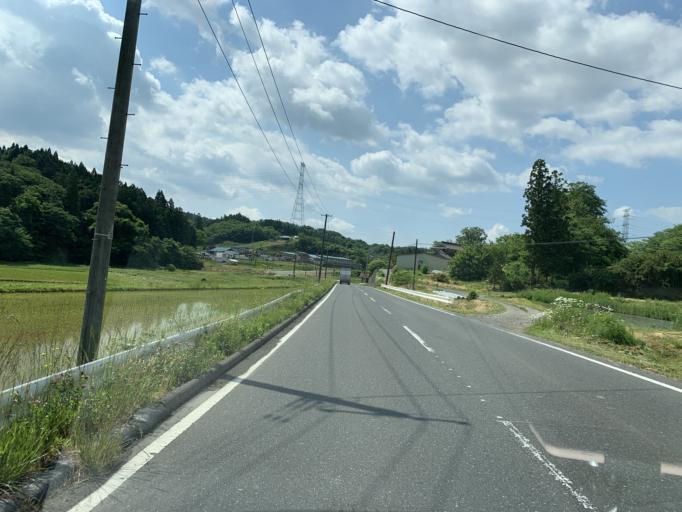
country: JP
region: Miyagi
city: Furukawa
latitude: 38.7835
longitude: 140.9580
